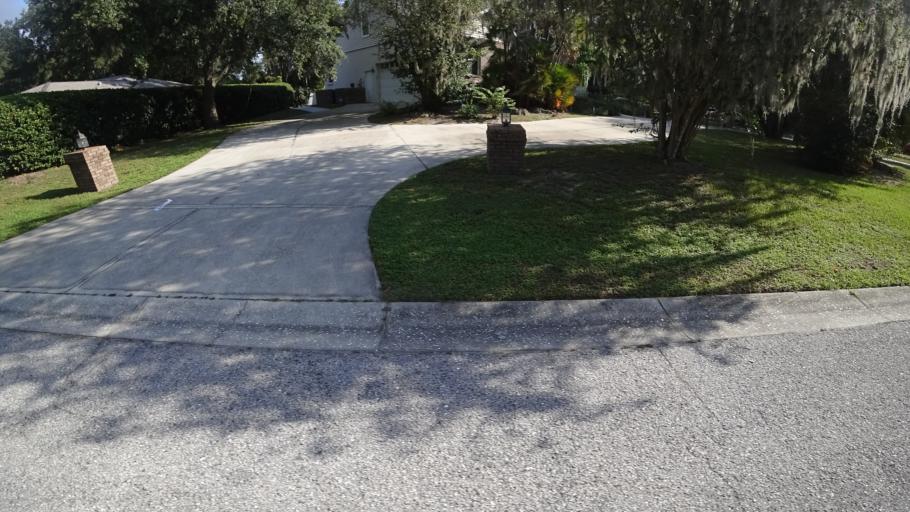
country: US
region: Florida
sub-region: Sarasota County
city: Desoto Lakes
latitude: 27.4302
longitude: -82.4518
